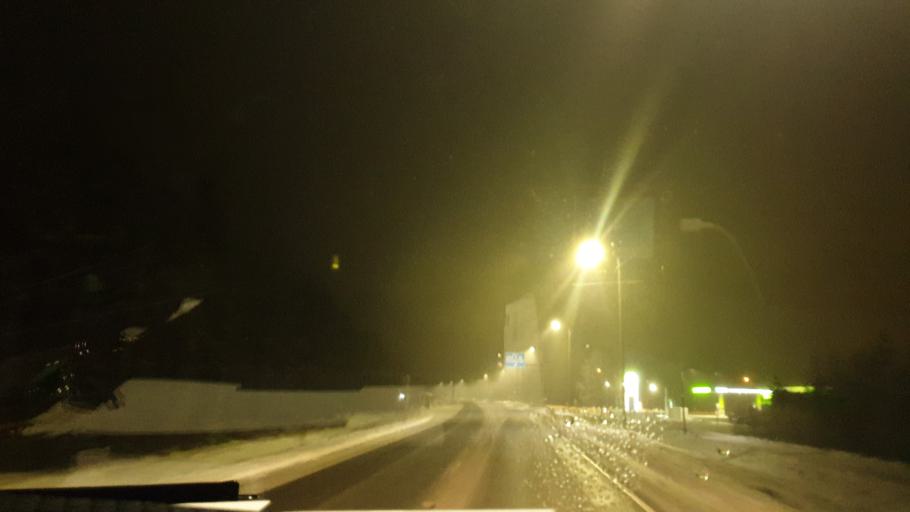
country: FI
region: Northern Ostrobothnia
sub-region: Oulunkaari
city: Kuivaniemi
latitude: 65.5874
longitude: 25.1966
